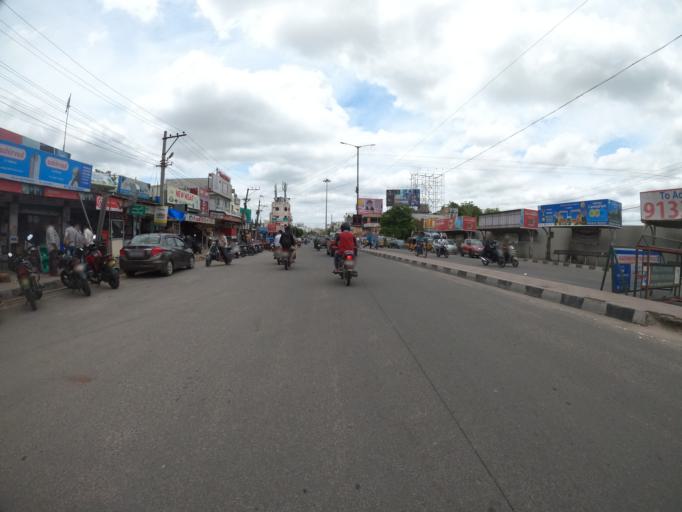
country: IN
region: Telangana
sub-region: Hyderabad
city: Hyderabad
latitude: 17.3856
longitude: 78.3549
